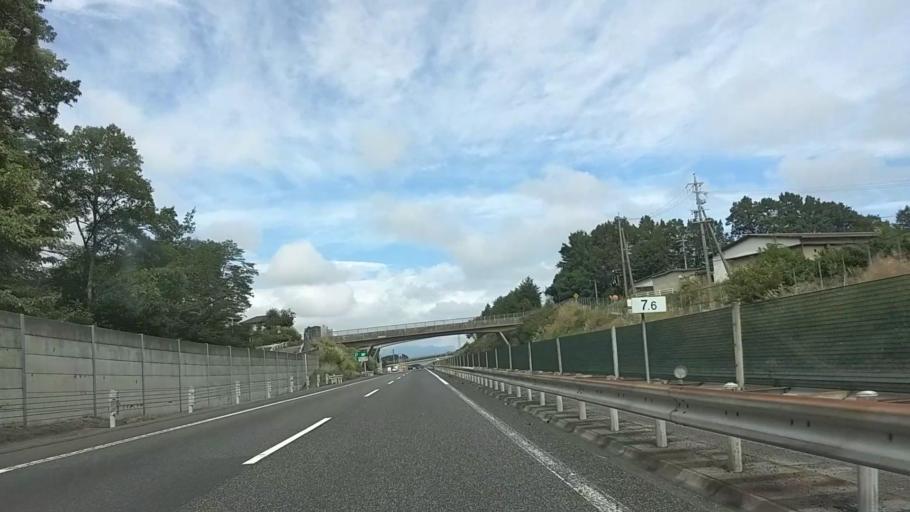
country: JP
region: Nagano
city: Shiojiri
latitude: 36.0933
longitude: 138.0010
